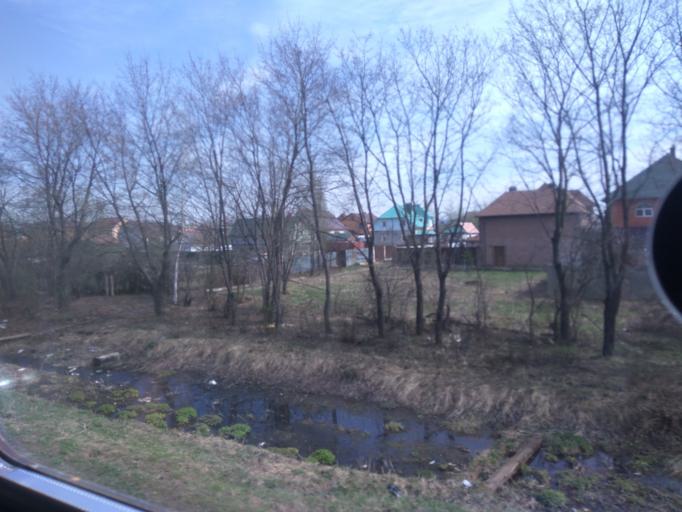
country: RU
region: Moskovskaya
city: Lobnya
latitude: 56.0032
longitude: 37.4899
